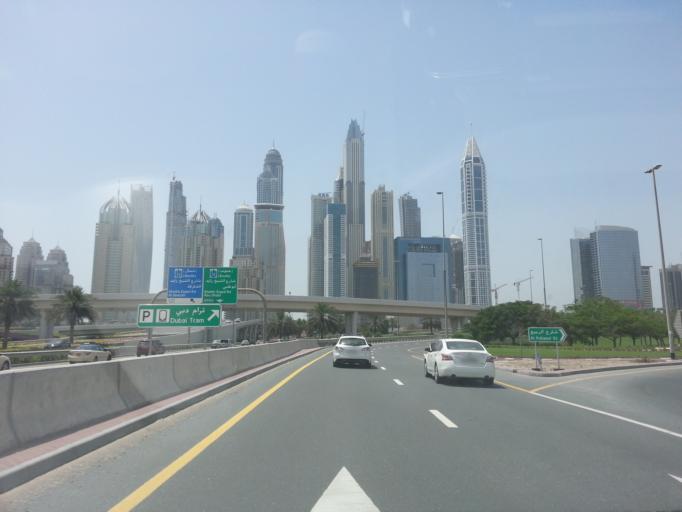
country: AE
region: Dubai
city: Dubai
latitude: 25.0815
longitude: 55.1551
